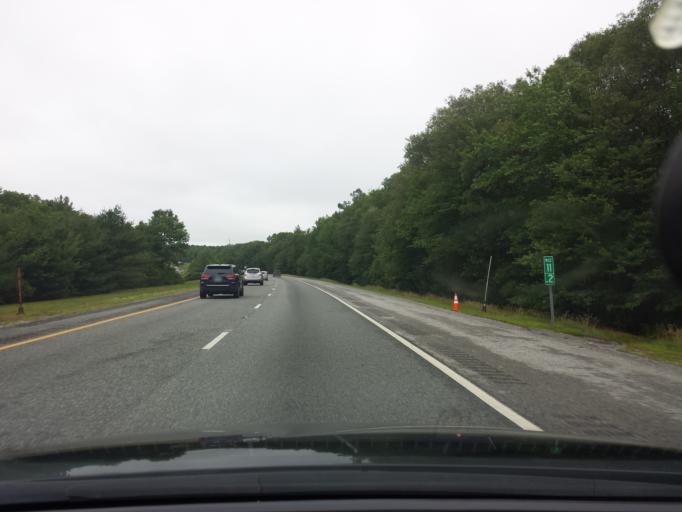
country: US
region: Rhode Island
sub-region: Kent County
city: West Greenwich
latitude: 41.5642
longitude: -71.6638
